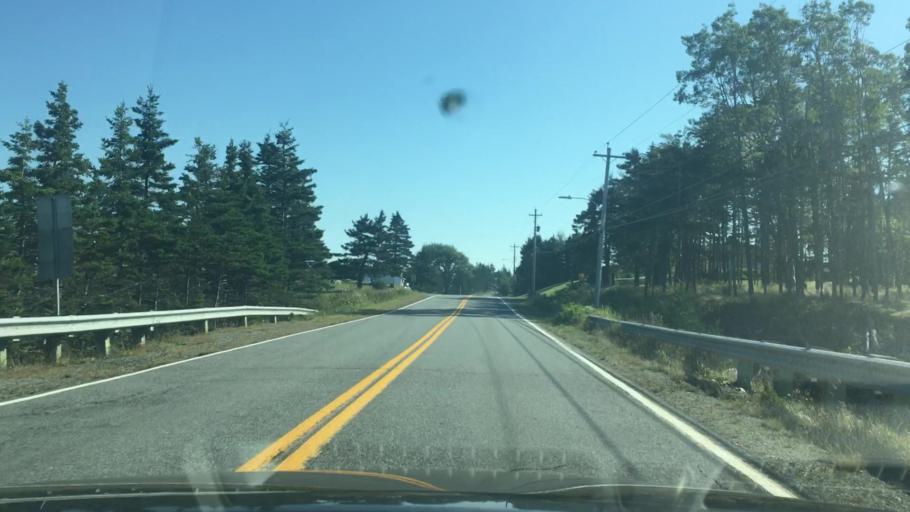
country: CA
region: Nova Scotia
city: Cole Harbour
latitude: 44.7779
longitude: -63.0121
